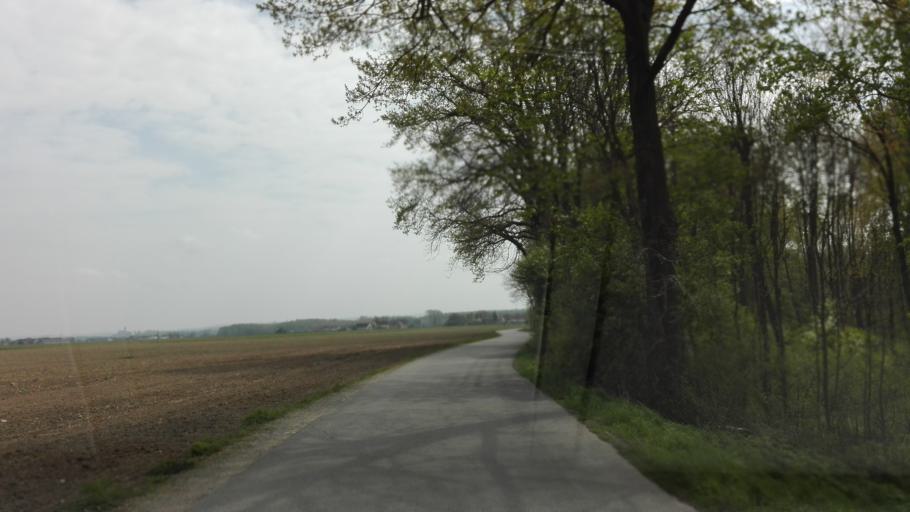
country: AT
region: Lower Austria
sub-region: Politischer Bezirk Amstetten
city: Strengberg
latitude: 48.1895
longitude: 14.6412
